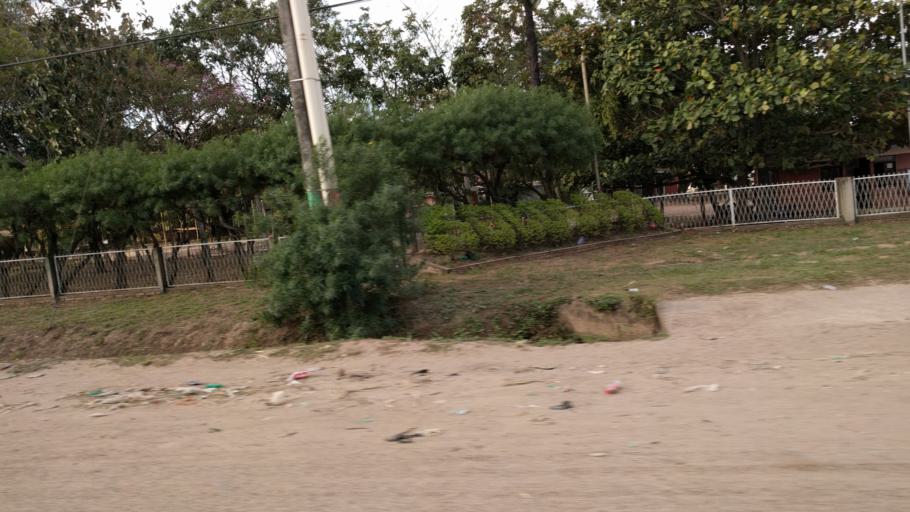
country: BO
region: Santa Cruz
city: Warnes
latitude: -17.5188
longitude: -63.1638
